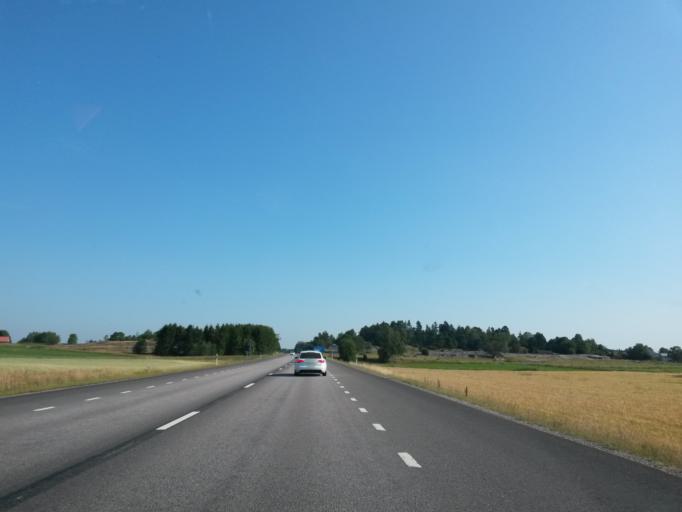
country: SE
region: Vaestra Goetaland
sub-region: Vargarda Kommun
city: Vargarda
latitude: 58.1364
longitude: 12.8609
